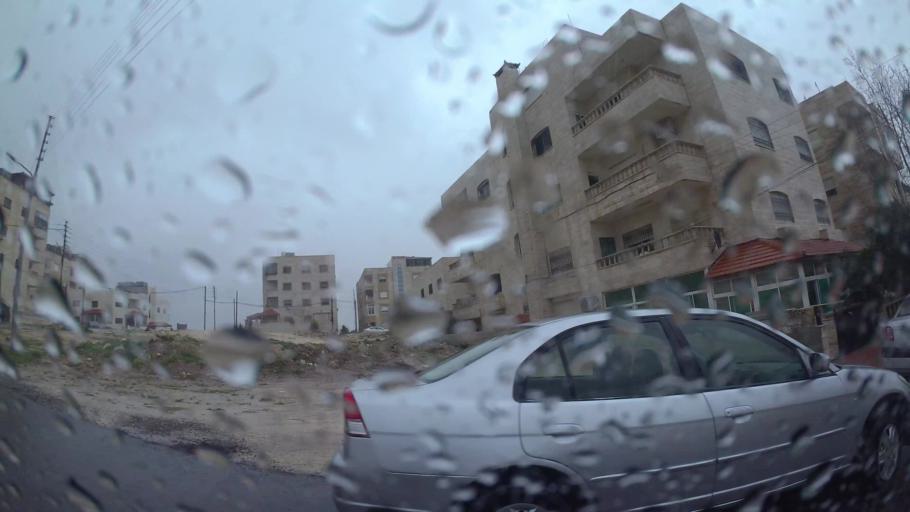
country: JO
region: Amman
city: Al Jubayhah
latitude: 32.0445
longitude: 35.8934
